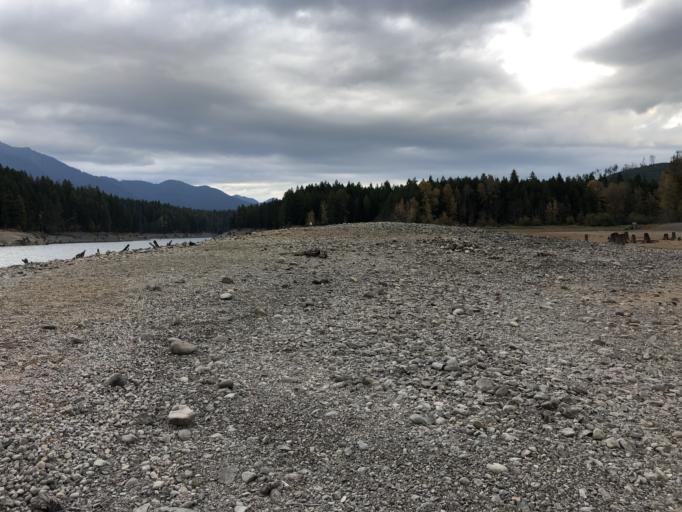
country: US
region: Washington
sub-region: Mason County
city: Shelton
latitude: 47.4623
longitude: -123.2254
